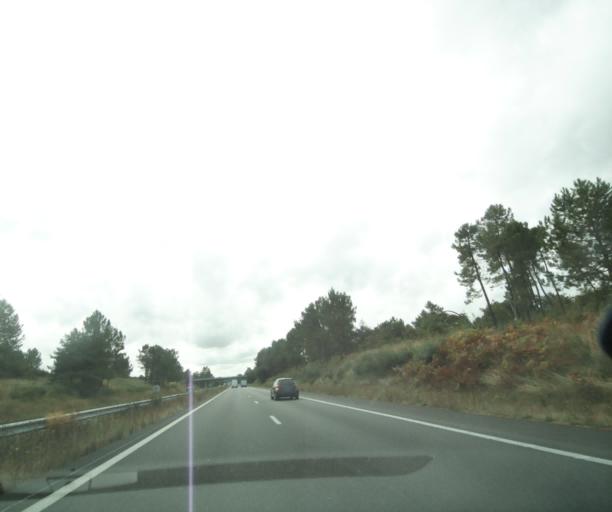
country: FR
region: Poitou-Charentes
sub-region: Departement de la Charente-Maritime
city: Saint-Genis-de-Saintonge
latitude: 45.4562
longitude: -0.6164
